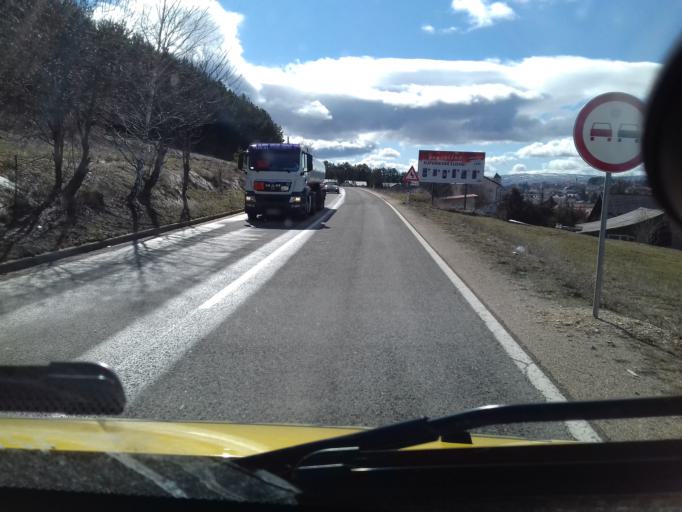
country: BA
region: Federation of Bosnia and Herzegovina
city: Tomislavgrad
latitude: 43.7262
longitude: 17.2244
